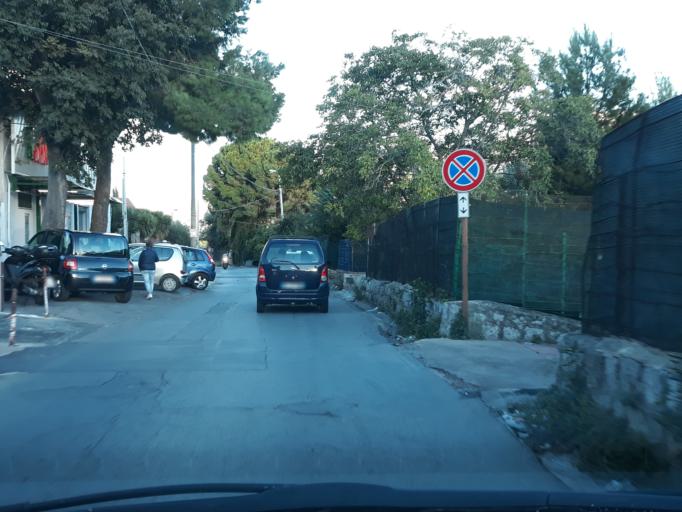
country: IT
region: Sicily
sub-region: Palermo
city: Monreale
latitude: 38.0747
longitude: 13.3048
